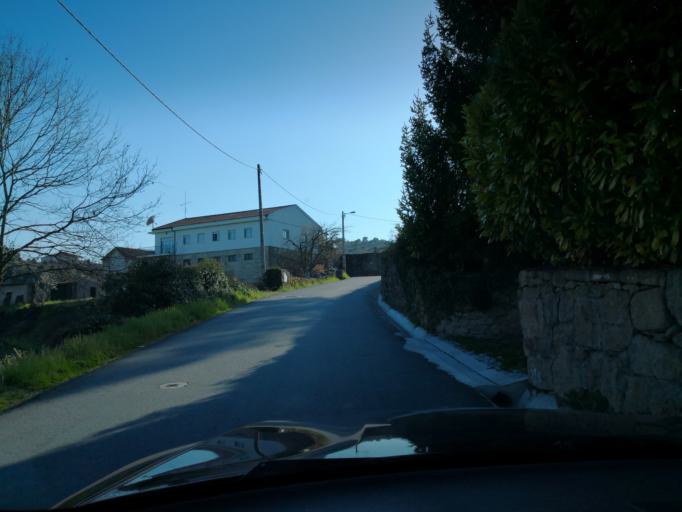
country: PT
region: Vila Real
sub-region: Vila Real
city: Vila Real
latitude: 41.2928
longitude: -7.7646
